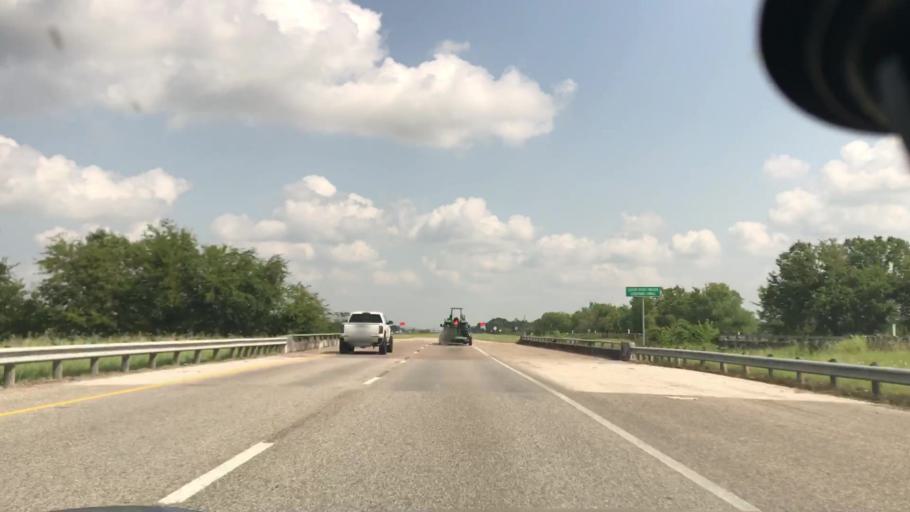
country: US
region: Texas
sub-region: Brazoria County
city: Rosharon
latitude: 29.3864
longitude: -95.4266
